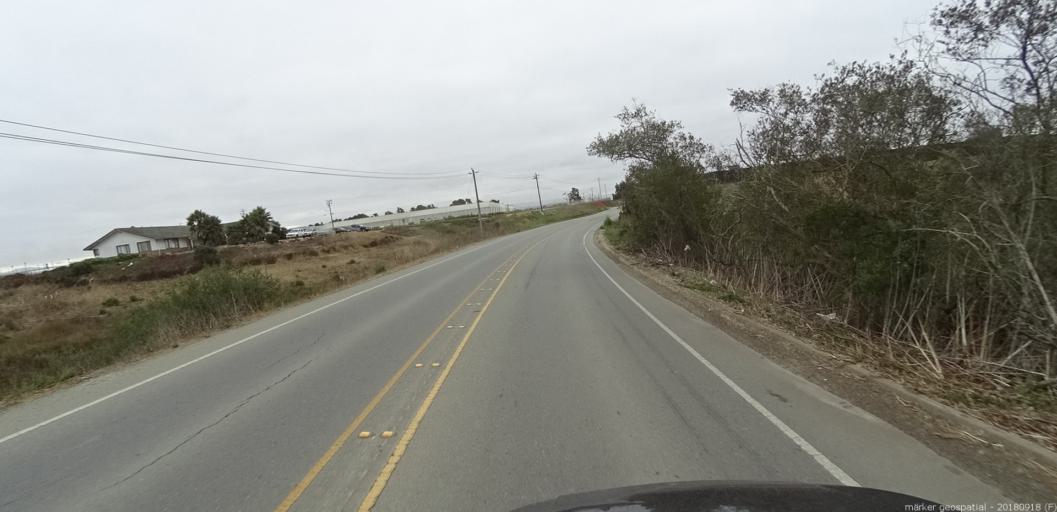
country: US
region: California
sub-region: Monterey County
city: Prunedale
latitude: 36.7463
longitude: -121.6967
